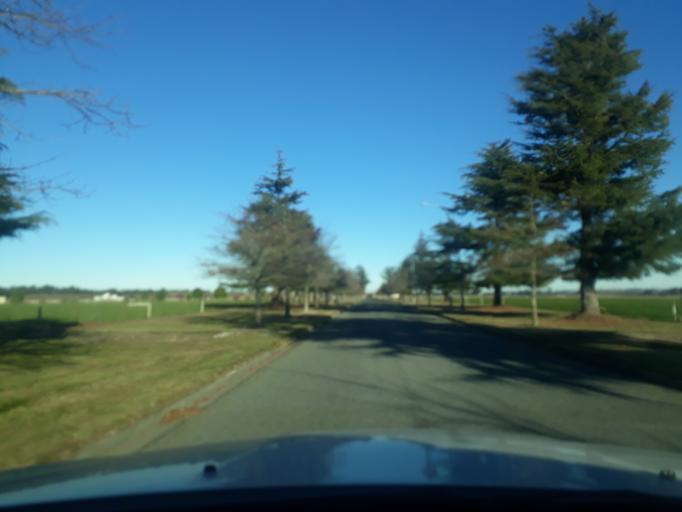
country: NZ
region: Canterbury
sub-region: Timaru District
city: Timaru
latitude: -44.3056
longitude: 171.2256
